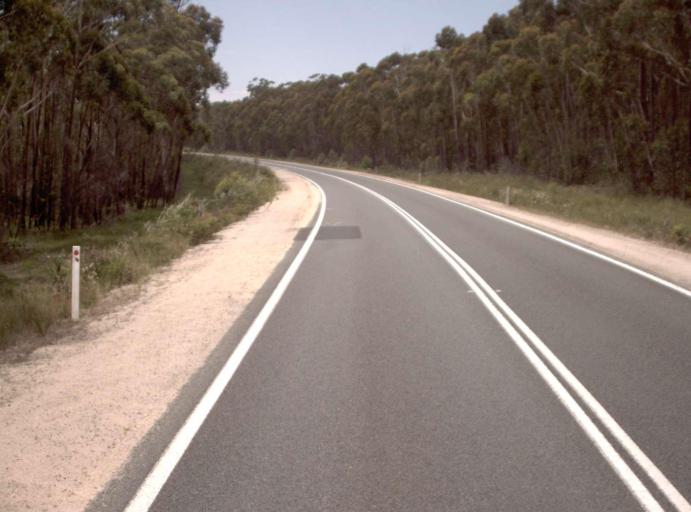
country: AU
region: New South Wales
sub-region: Bega Valley
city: Eden
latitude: -37.5336
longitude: 149.4838
